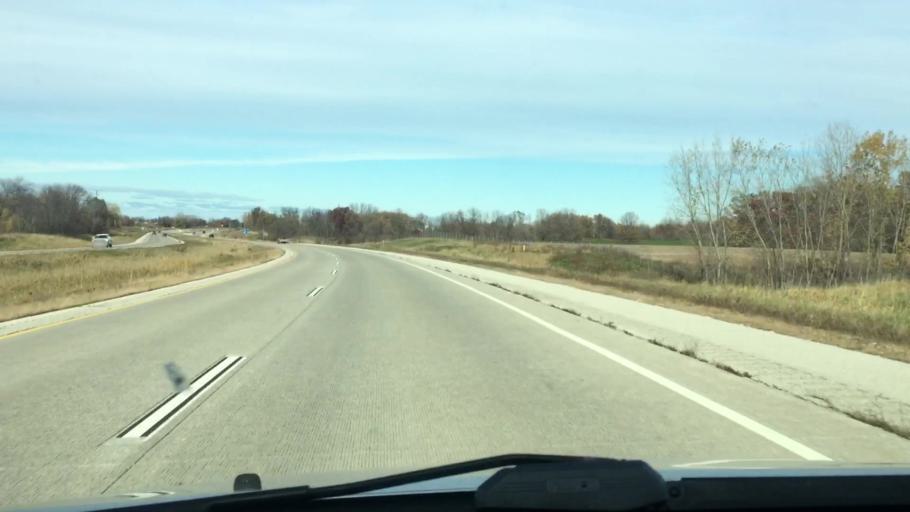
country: US
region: Wisconsin
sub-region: Kewaunee County
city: Luxemburg
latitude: 44.6403
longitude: -87.7535
